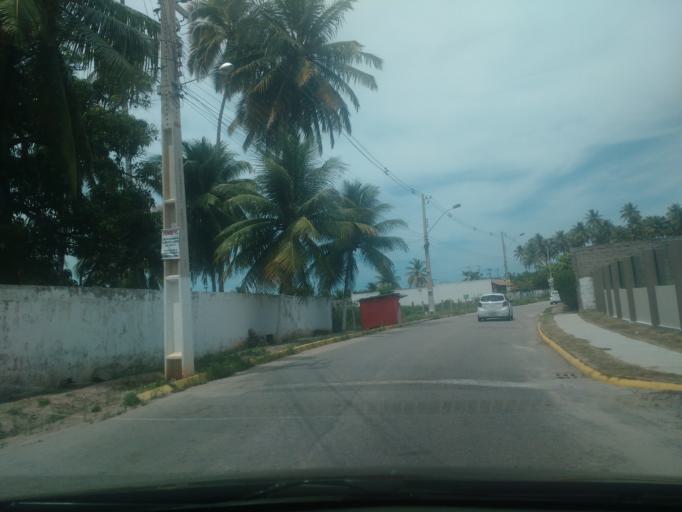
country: BR
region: Alagoas
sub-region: Marechal Deodoro
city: Marechal Deodoro
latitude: -9.7361
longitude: -35.8310
